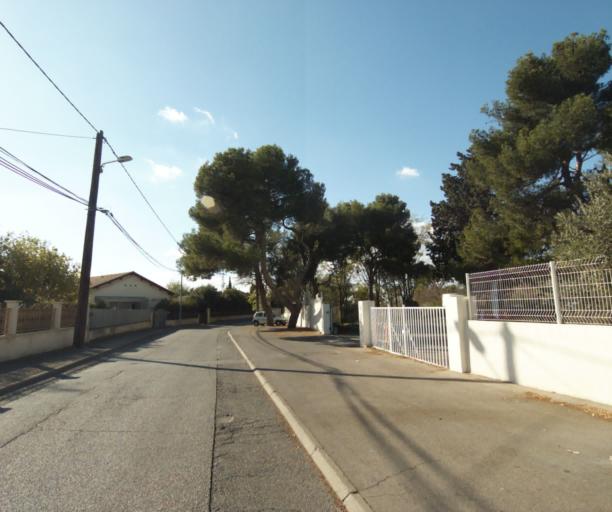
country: FR
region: Provence-Alpes-Cote d'Azur
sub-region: Departement des Bouches-du-Rhone
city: Saint-Victoret
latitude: 43.4104
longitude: 5.2477
